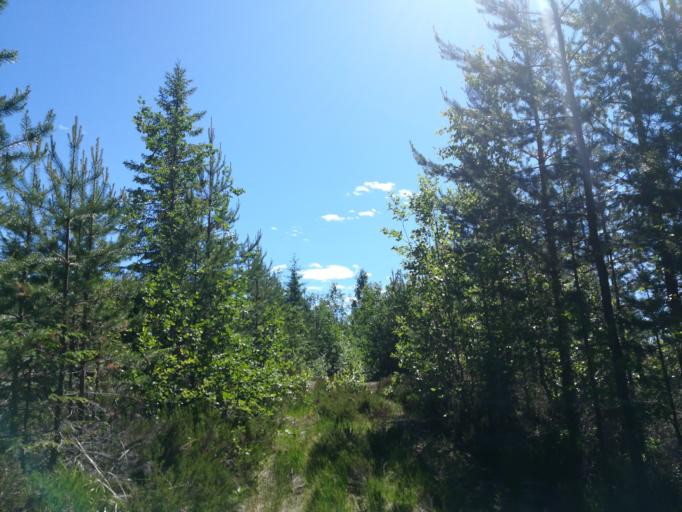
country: FI
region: Southern Savonia
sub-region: Mikkeli
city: Puumala
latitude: 61.6202
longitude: 28.1614
